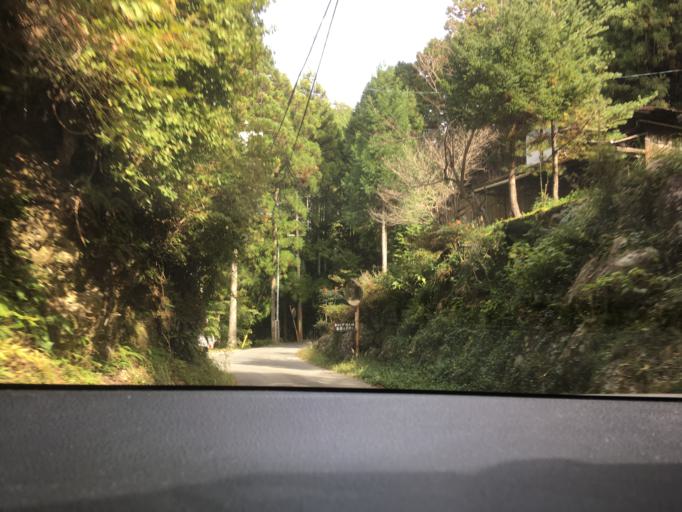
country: JP
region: Nara
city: Yoshino-cho
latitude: 34.3899
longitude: 135.9891
